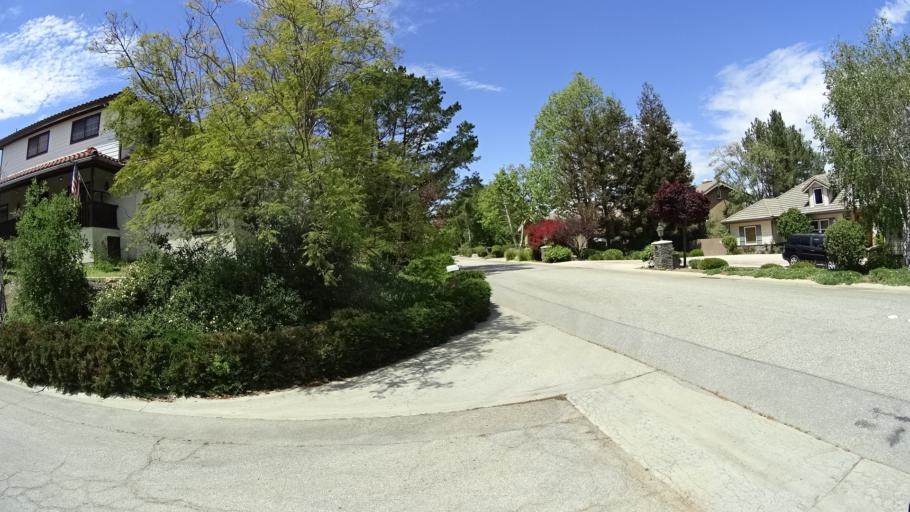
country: US
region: California
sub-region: Ventura County
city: Casa Conejo
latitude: 34.1727
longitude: -118.9233
